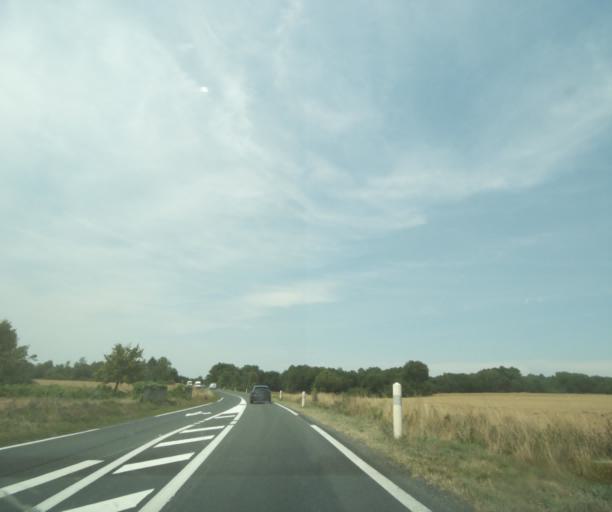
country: FR
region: Poitou-Charentes
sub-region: Departement de la Vienne
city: Chauvigny
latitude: 46.5454
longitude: 0.6432
